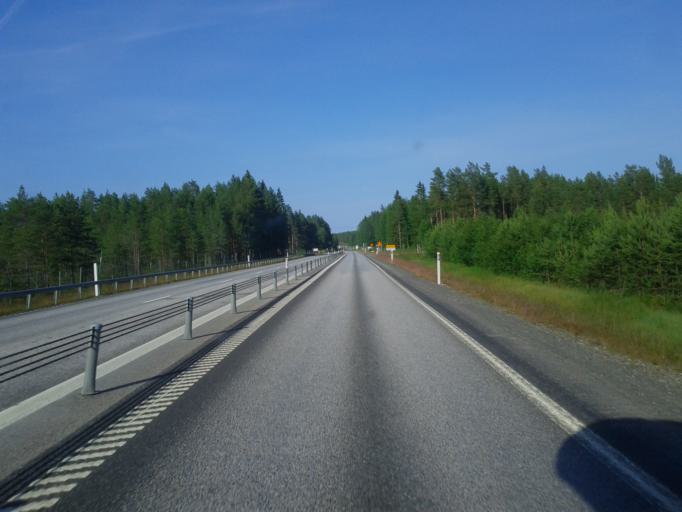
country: SE
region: Vaesterbotten
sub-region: Robertsfors Kommun
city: Robertsfors
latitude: 63.9928
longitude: 20.7638
